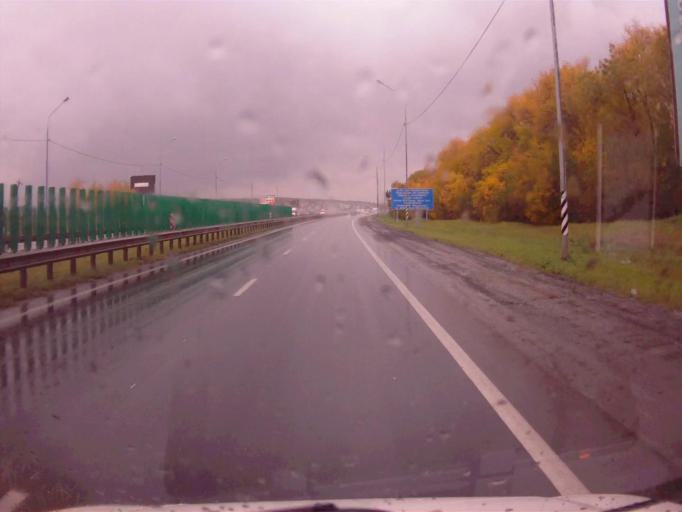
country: RU
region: Chelyabinsk
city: Dolgoderevenskoye
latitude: 55.2674
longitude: 61.3454
